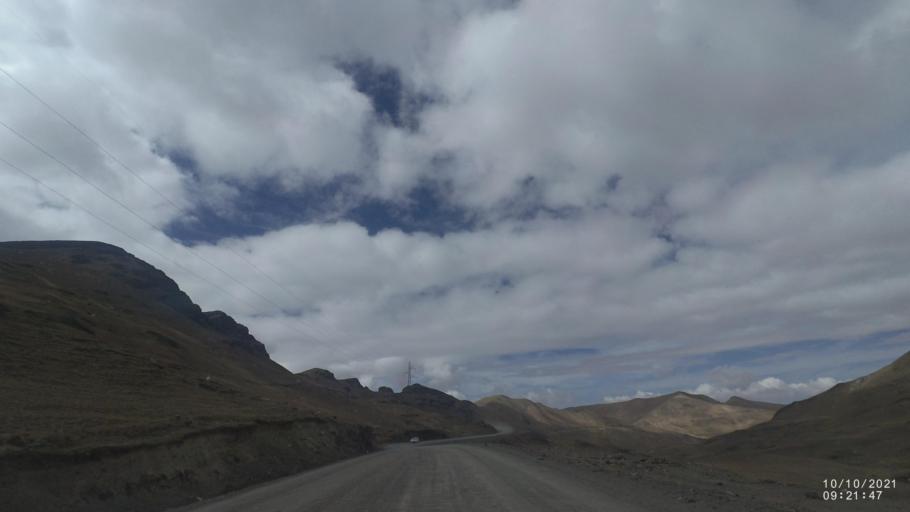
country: BO
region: La Paz
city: Quime
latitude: -17.0711
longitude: -67.2988
